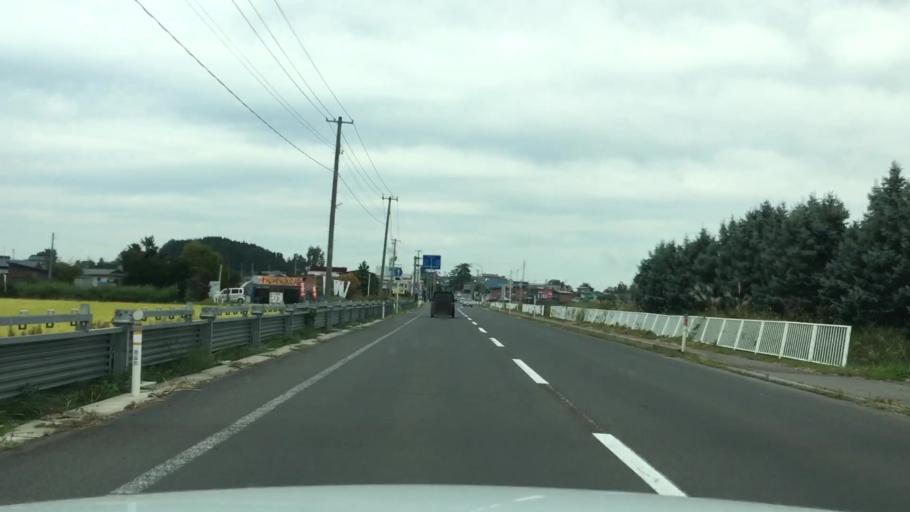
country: JP
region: Aomori
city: Hirosaki
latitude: 40.6390
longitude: 140.4470
